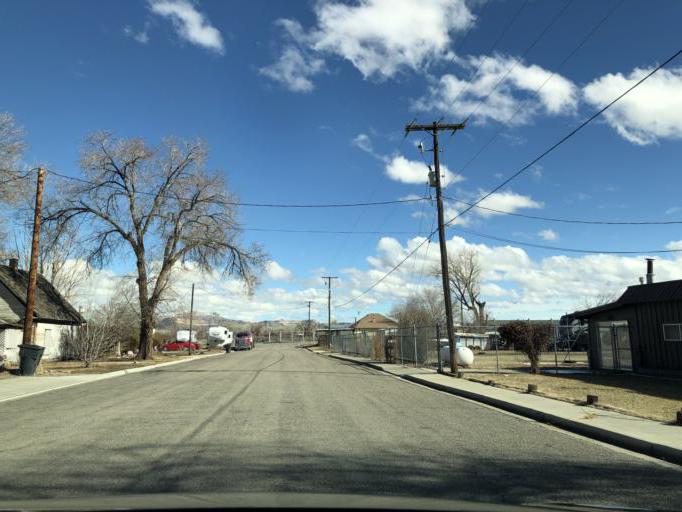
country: US
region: Utah
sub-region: Carbon County
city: East Carbon City
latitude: 38.9970
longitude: -110.1597
